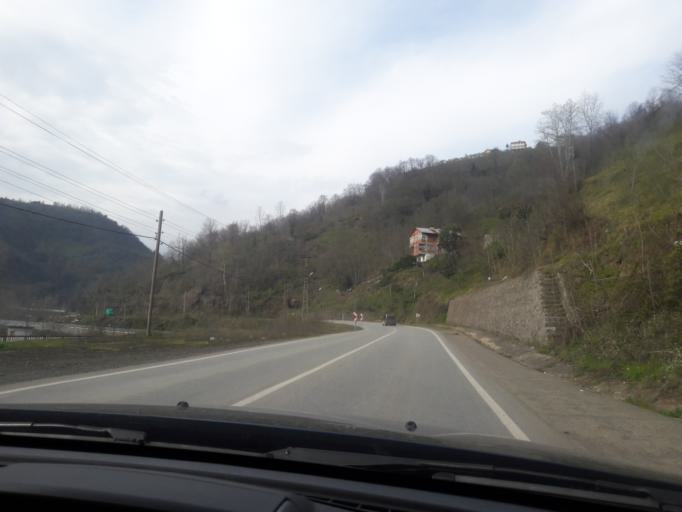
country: TR
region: Trabzon
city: Besikduzu
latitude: 41.0521
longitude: 39.2068
